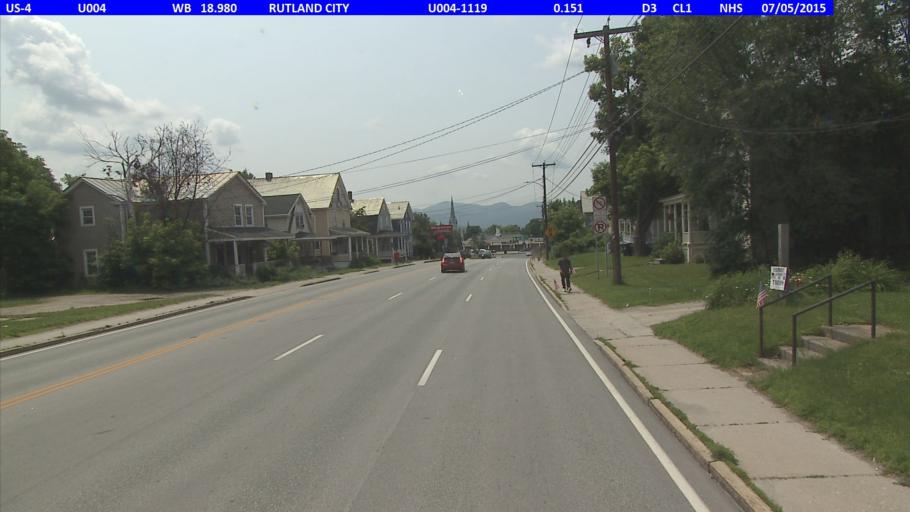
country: US
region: Vermont
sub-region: Rutland County
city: Rutland
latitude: 43.6113
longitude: -72.9699
